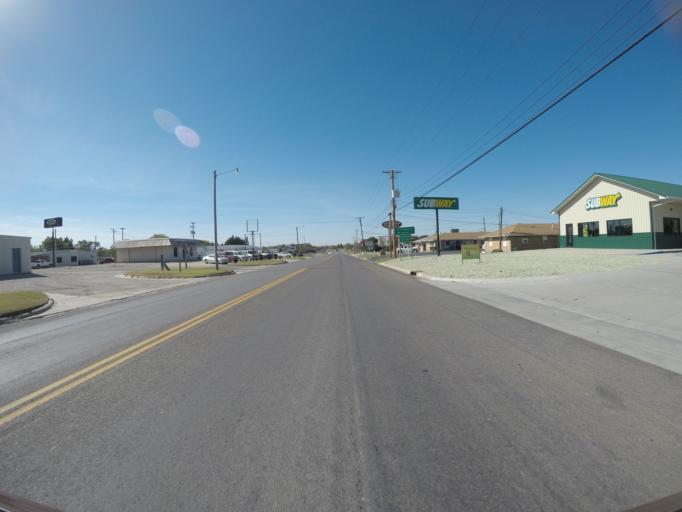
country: US
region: Kansas
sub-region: Smith County
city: Smith Center
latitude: 39.7852
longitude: -98.7841
